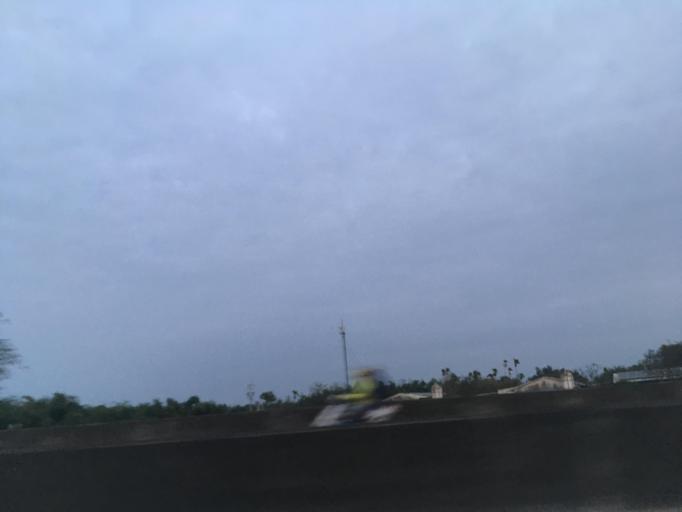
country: TW
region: Taiwan
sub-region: Chiayi
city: Jiayi Shi
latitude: 23.5940
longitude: 120.4645
